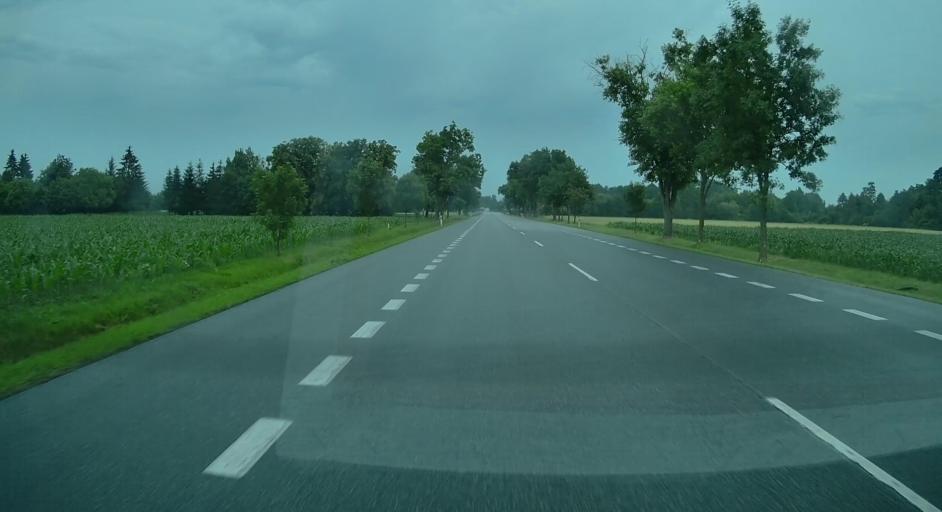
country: PL
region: Masovian Voivodeship
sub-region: Powiat siedlecki
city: Zbuczyn
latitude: 52.0708
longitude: 22.5133
